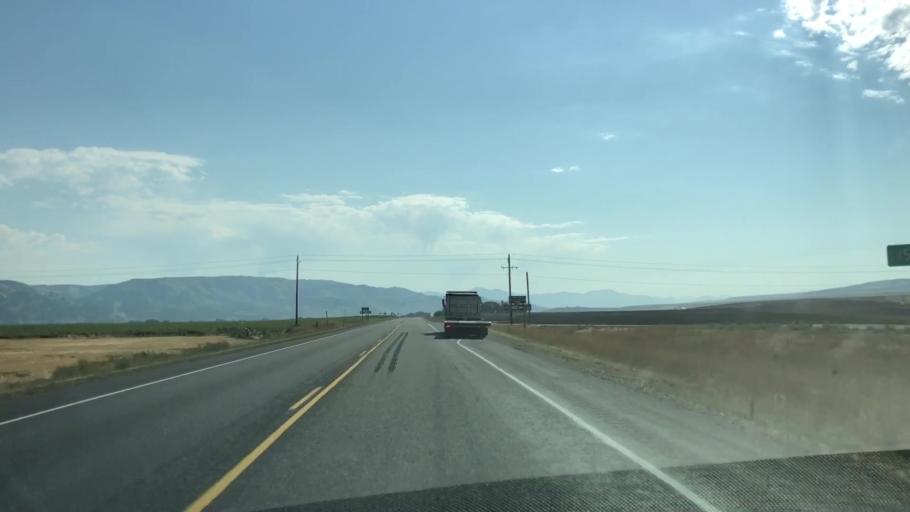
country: US
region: Idaho
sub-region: Jefferson County
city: Rigby
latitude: 43.6140
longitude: -111.7504
